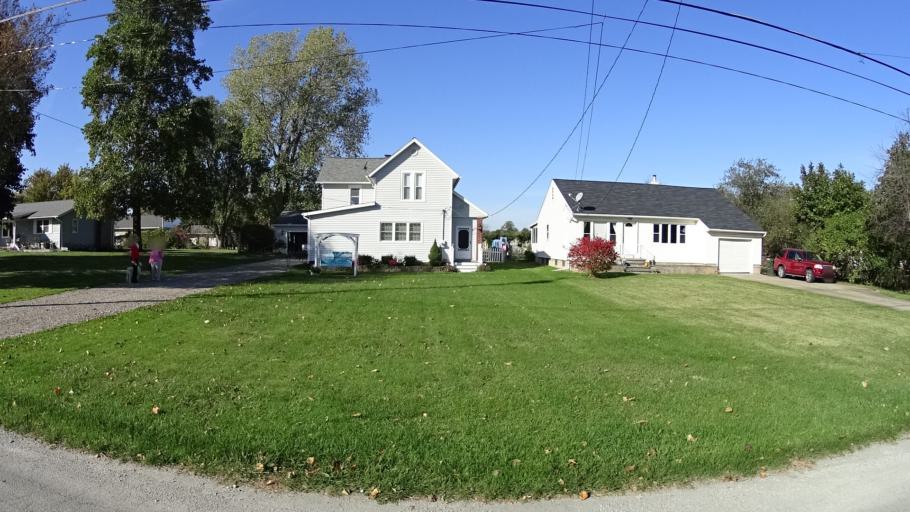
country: US
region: Ohio
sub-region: Lorain County
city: Vermilion-on-the-Lake
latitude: 41.4266
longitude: -82.2983
